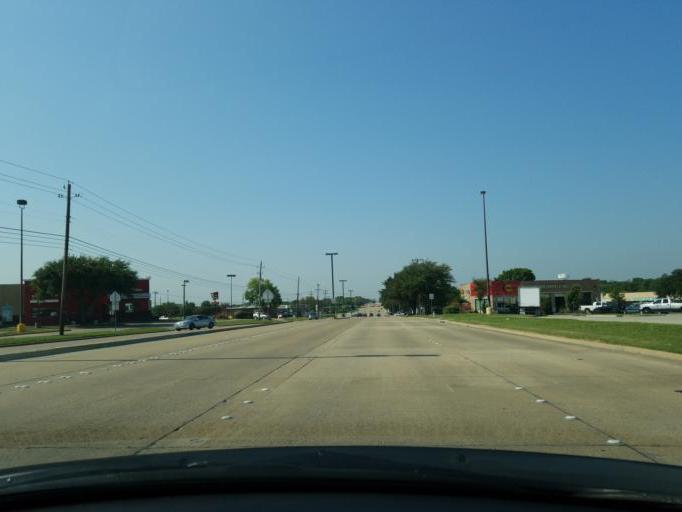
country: US
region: Texas
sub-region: Collin County
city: Allen
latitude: 33.1026
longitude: -96.6605
